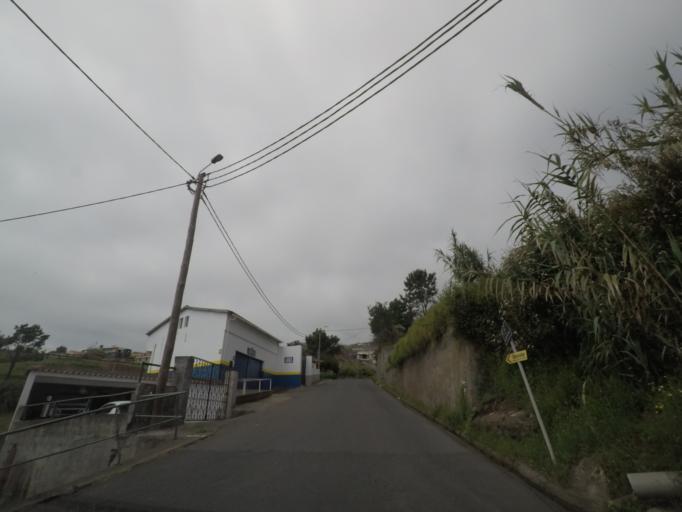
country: PT
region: Madeira
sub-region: Calheta
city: Arco da Calheta
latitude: 32.7060
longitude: -17.1132
